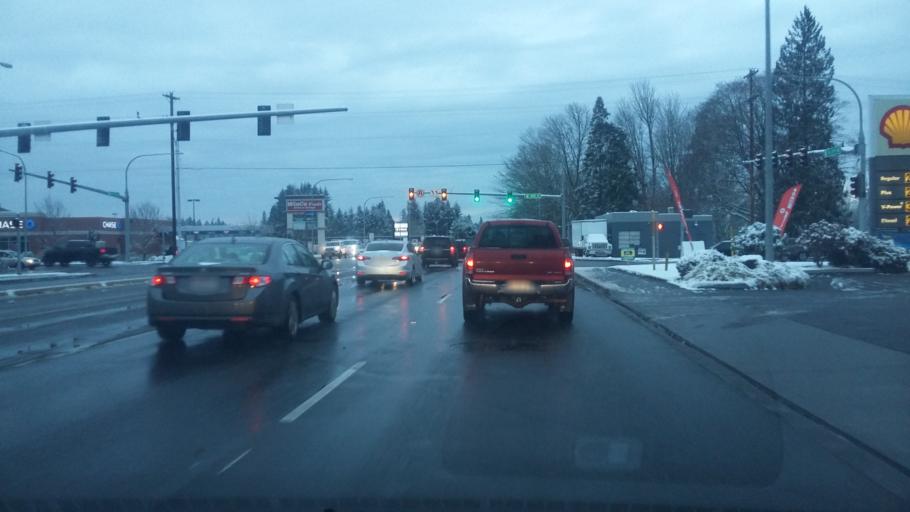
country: US
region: Washington
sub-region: Clark County
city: Brush Prairie
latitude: 45.7074
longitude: -122.5526
